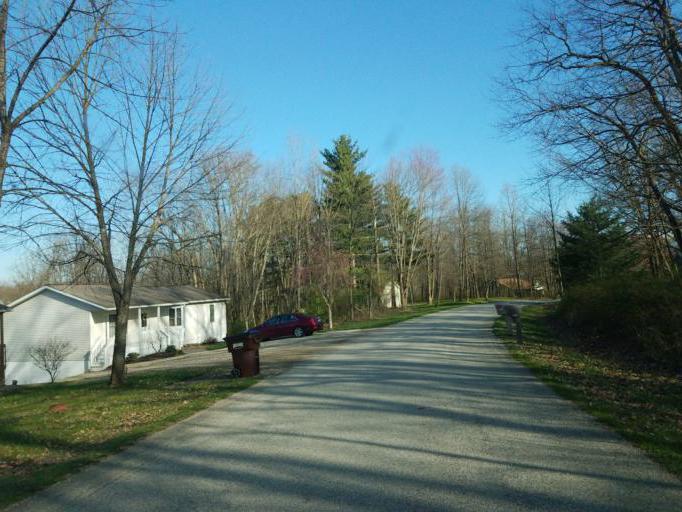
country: US
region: Ohio
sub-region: Knox County
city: Danville
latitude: 40.4483
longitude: -82.3460
